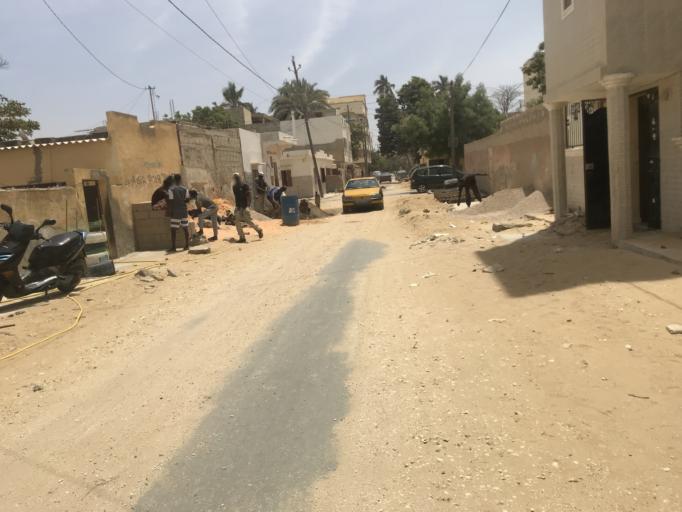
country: SN
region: Saint-Louis
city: Saint-Louis
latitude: 16.0230
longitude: -16.4867
